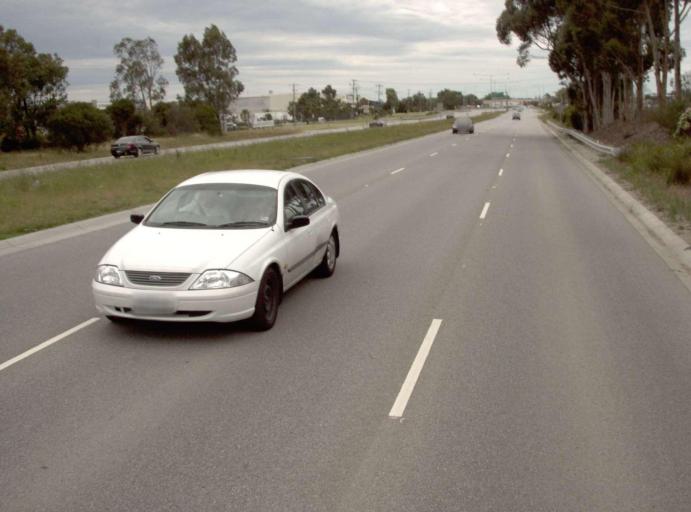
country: AU
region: Victoria
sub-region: Casey
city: Hampton Park
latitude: -38.0319
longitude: 145.2444
